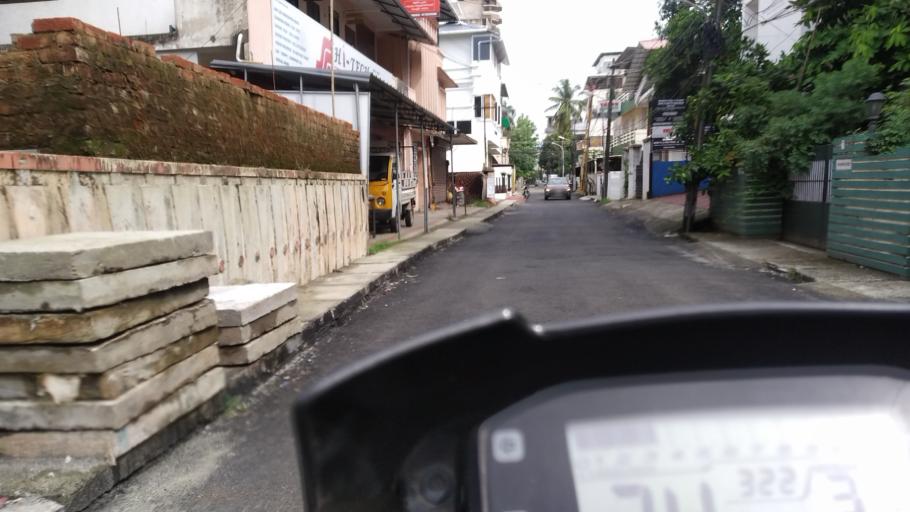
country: IN
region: Kerala
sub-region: Ernakulam
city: Cochin
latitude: 9.9908
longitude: 76.2804
